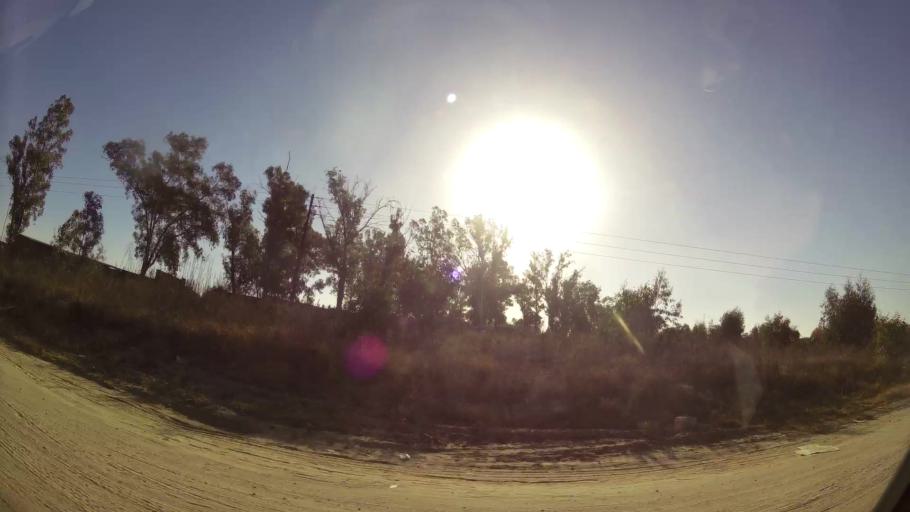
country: ZA
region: Gauteng
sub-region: City of Johannesburg Metropolitan Municipality
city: Diepsloot
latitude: -25.9490
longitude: 27.9660
